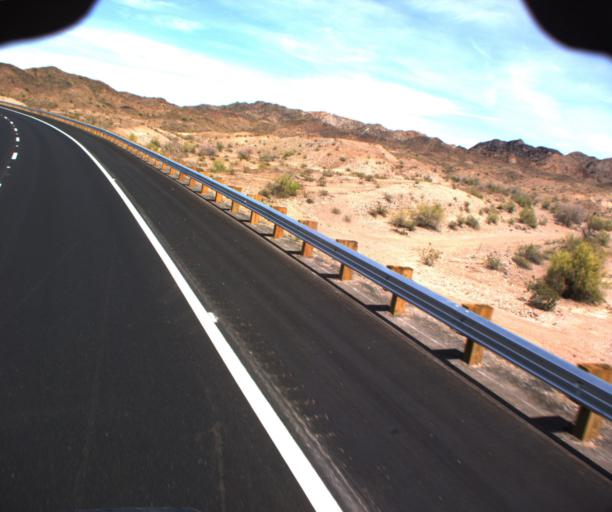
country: US
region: Arizona
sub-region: La Paz County
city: Cienega Springs
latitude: 34.1908
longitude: -114.2098
